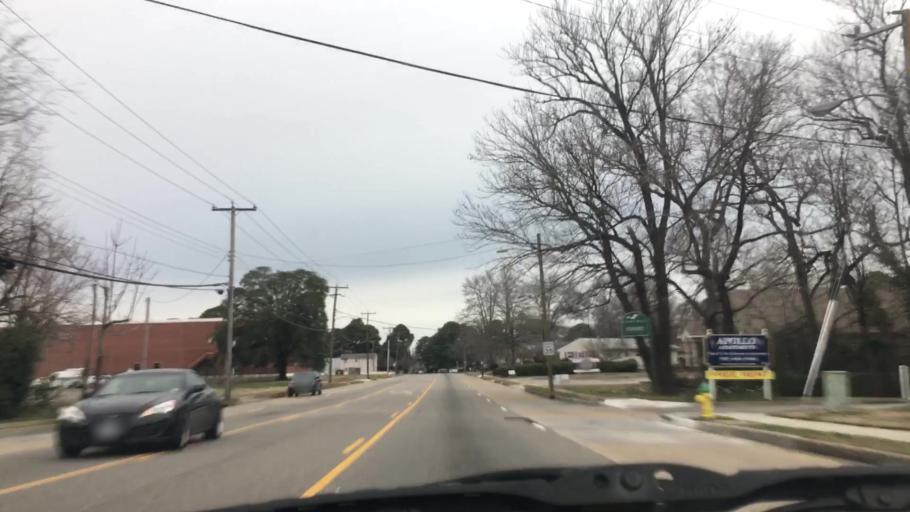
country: US
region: Virginia
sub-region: City of Norfolk
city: Norfolk
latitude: 36.8792
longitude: -76.2334
